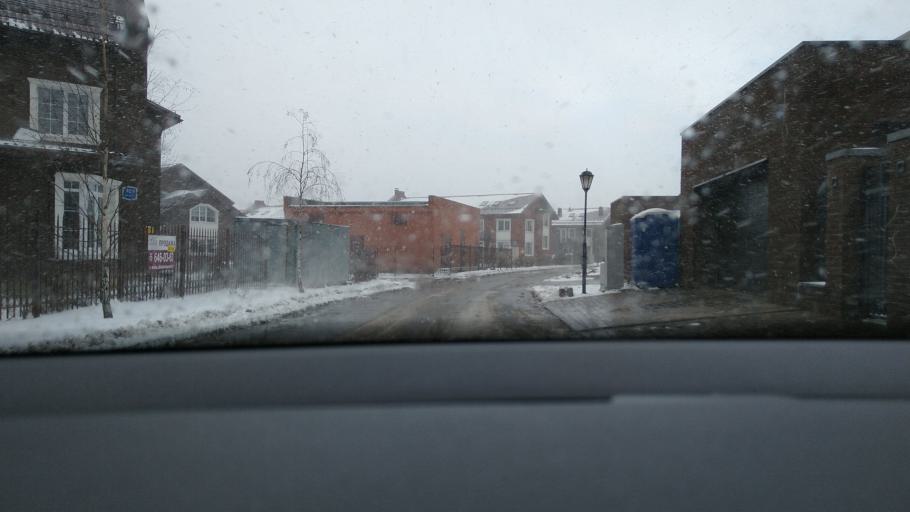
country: RU
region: Moskovskaya
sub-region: Leninskiy Rayon
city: Vnukovo
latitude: 55.6173
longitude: 37.3203
